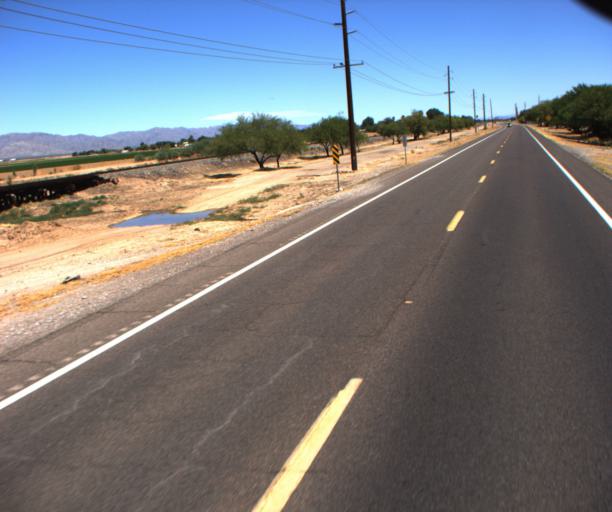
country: US
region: Arizona
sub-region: La Paz County
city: Salome
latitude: 33.8177
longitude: -113.5498
